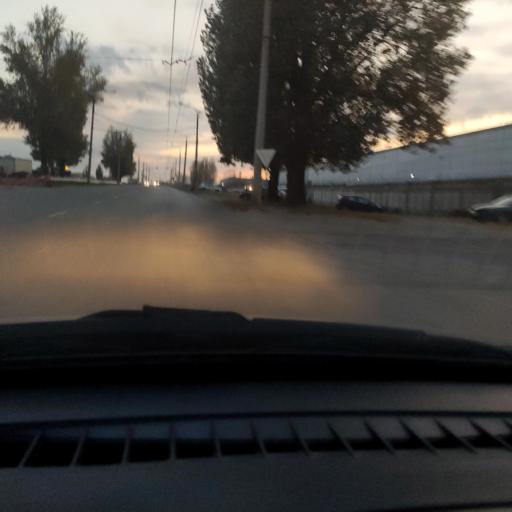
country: RU
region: Samara
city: Povolzhskiy
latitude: 53.5474
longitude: 49.6106
